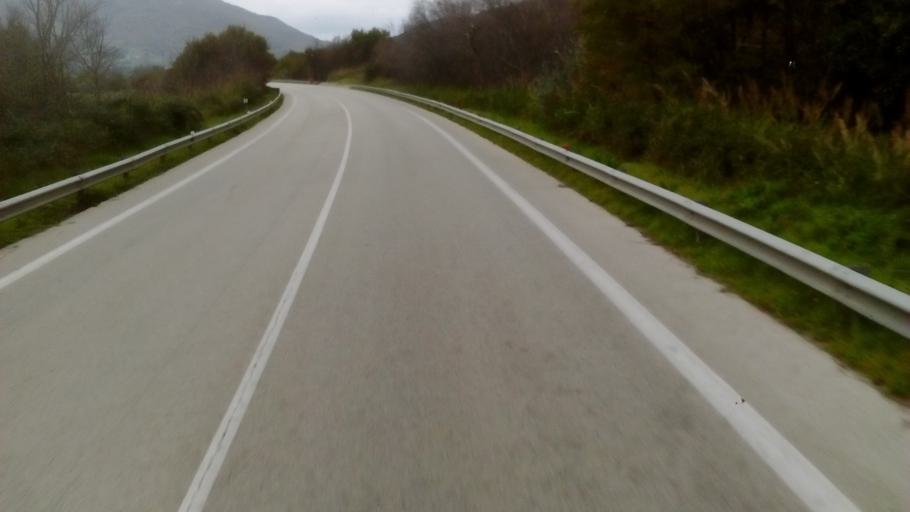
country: IT
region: Abruzzo
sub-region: Provincia di Chieti
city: Celenza sul Trigno
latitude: 41.8764
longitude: 14.6042
